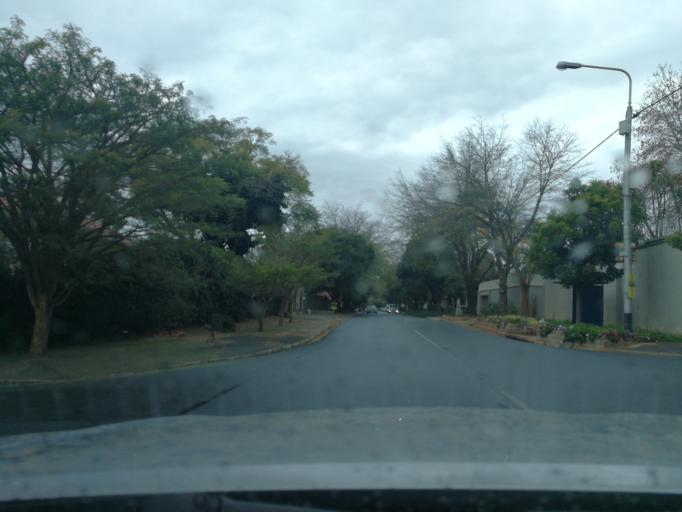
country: ZA
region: Gauteng
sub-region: City of Johannesburg Metropolitan Municipality
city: Johannesburg
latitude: -26.1568
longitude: 28.0170
